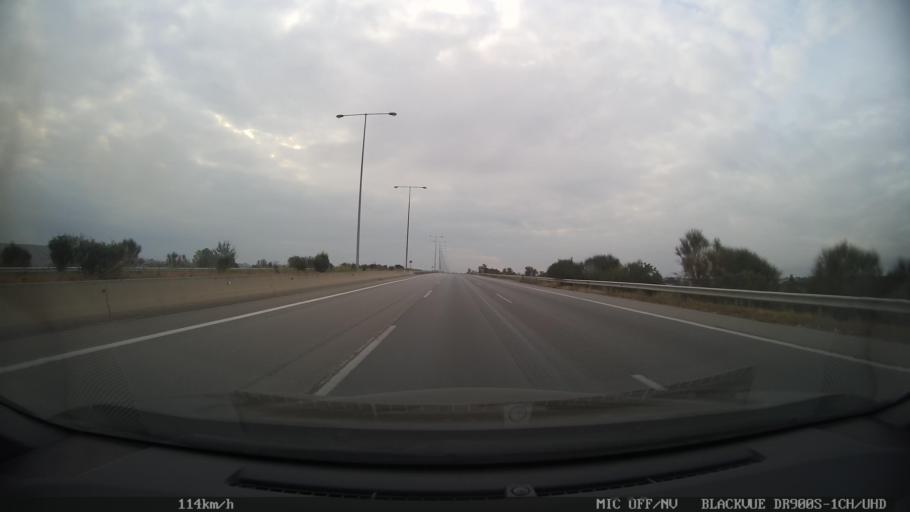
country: GR
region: Central Macedonia
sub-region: Nomos Thessalonikis
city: Nea Magnisia
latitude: 40.6700
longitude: 22.8339
